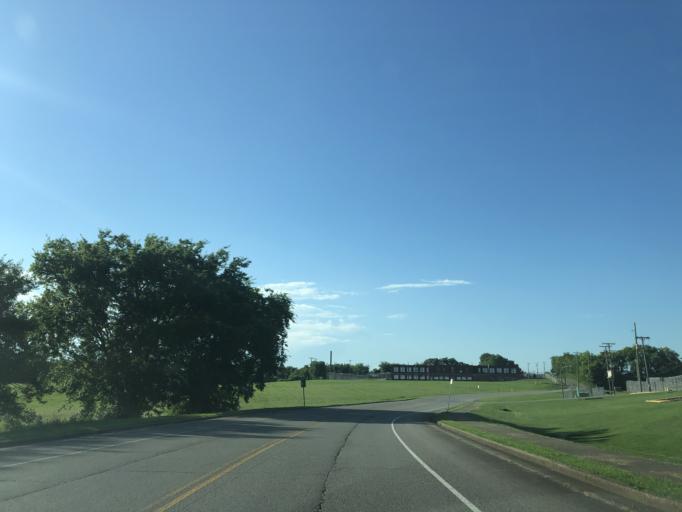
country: US
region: Tennessee
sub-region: Davidson County
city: Nashville
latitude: 36.1919
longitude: -86.8631
